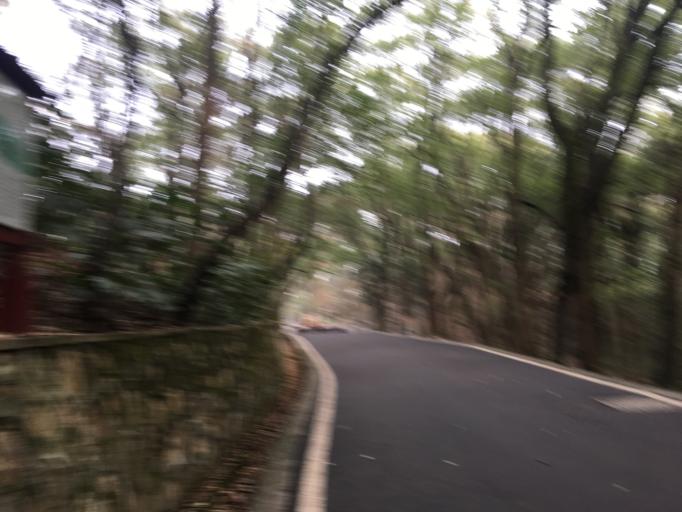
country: CN
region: Hubei
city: Guanshan
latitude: 30.5372
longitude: 114.3688
